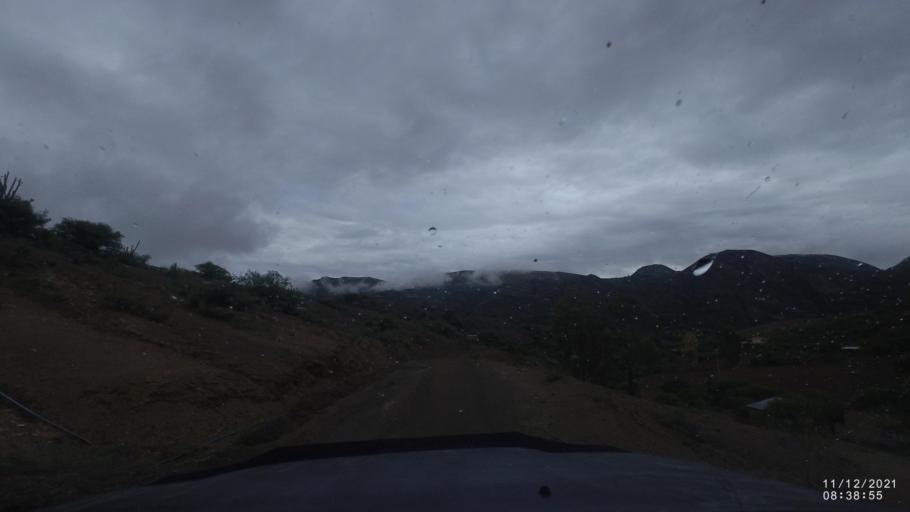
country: BO
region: Cochabamba
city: Tarata
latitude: -17.9226
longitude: -65.9363
